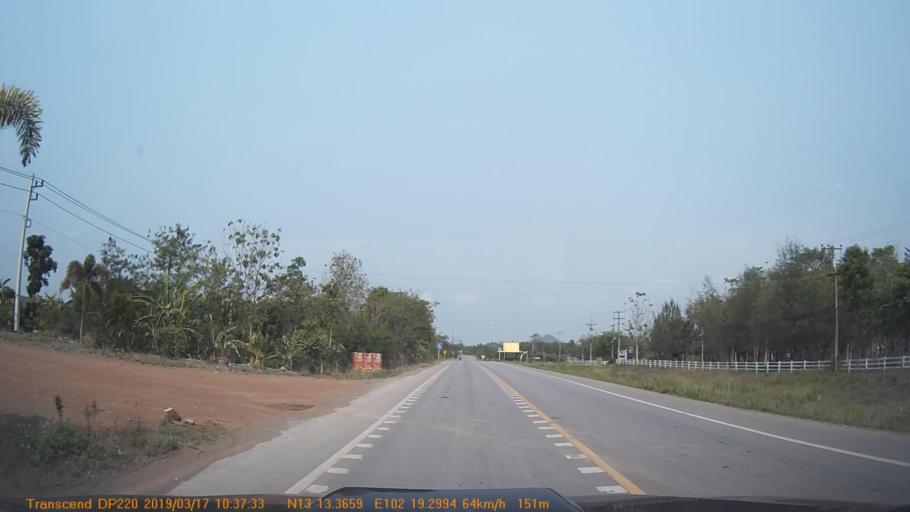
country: TH
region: Chanthaburi
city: Soi Dao
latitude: 13.2228
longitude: 102.3215
